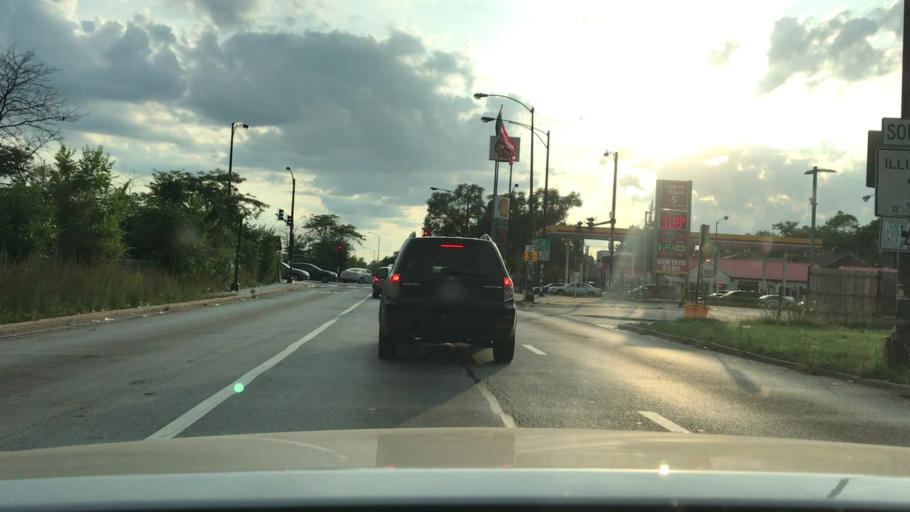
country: US
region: Illinois
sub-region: Cook County
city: Calumet Park
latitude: 41.7152
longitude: -87.6421
